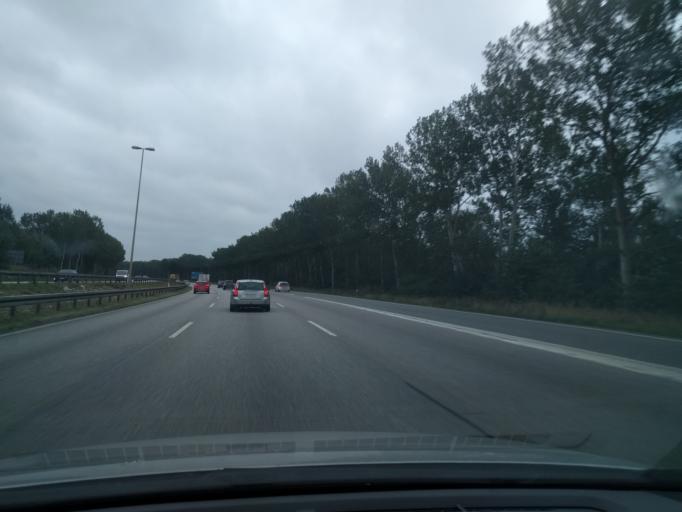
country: DK
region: Capital Region
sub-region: Hvidovre Kommune
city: Hvidovre
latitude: 55.6287
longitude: 12.4485
